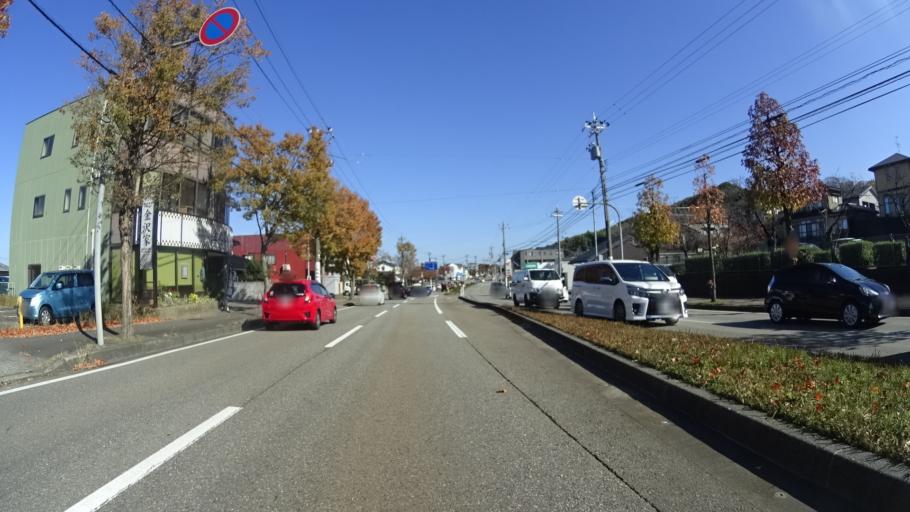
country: JP
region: Ishikawa
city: Nonoichi
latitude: 36.5166
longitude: 136.6323
